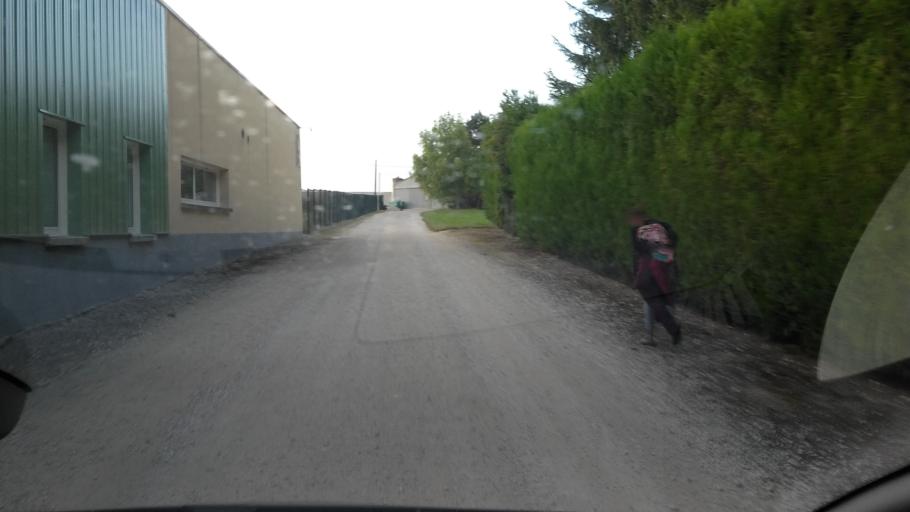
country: FR
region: Champagne-Ardenne
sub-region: Departement de la Marne
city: Fere-Champenoise
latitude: 48.7586
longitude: 3.9923
